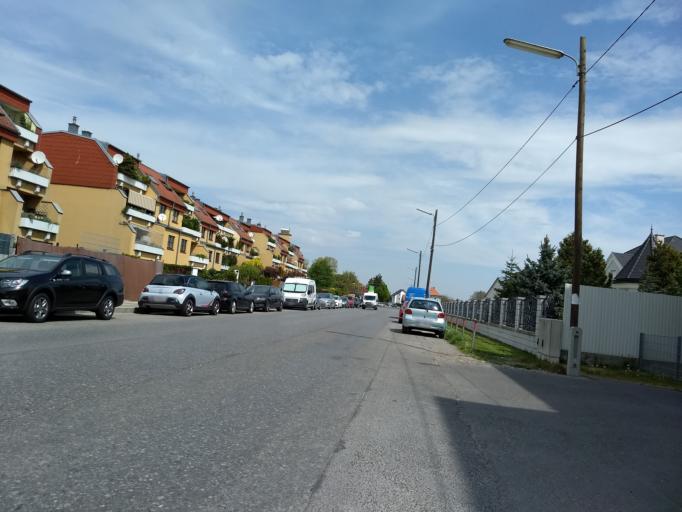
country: AT
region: Lower Austria
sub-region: Politischer Bezirk Wien-Umgebung
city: Gerasdorf bei Wien
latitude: 48.2380
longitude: 16.4896
